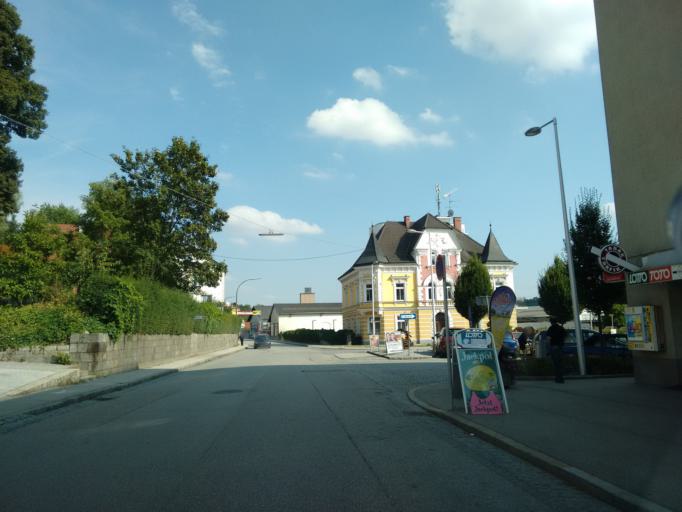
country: AT
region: Upper Austria
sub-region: Politischer Bezirk Grieskirchen
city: Grieskirchen
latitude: 48.2322
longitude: 13.8391
